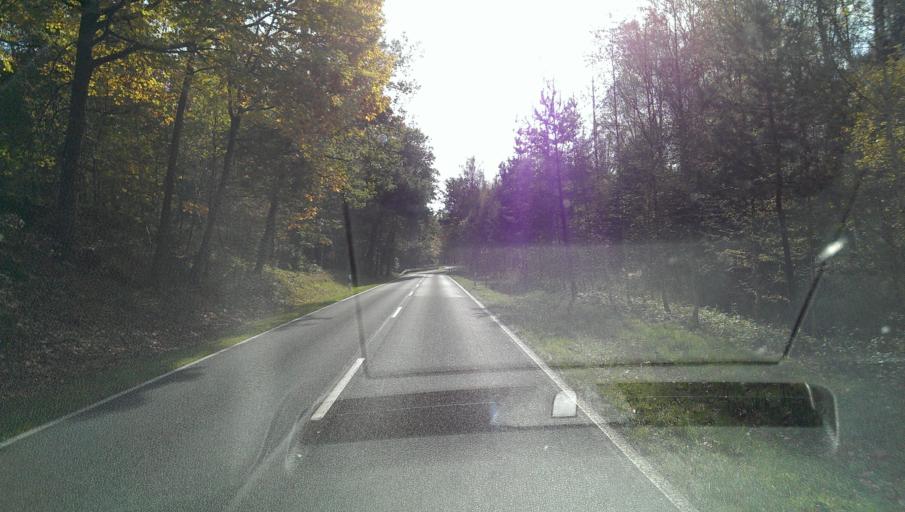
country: DE
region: Brandenburg
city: Lauchhammer
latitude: 51.5031
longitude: 13.7229
